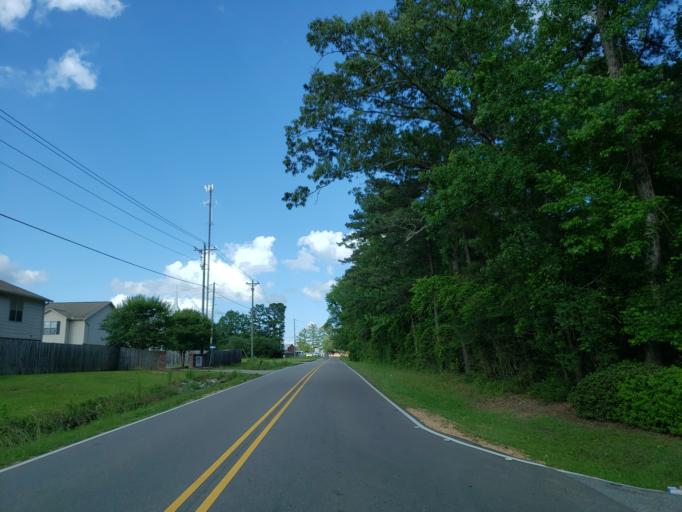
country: US
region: Mississippi
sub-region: Lamar County
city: West Hattiesburg
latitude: 31.2847
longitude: -89.4237
